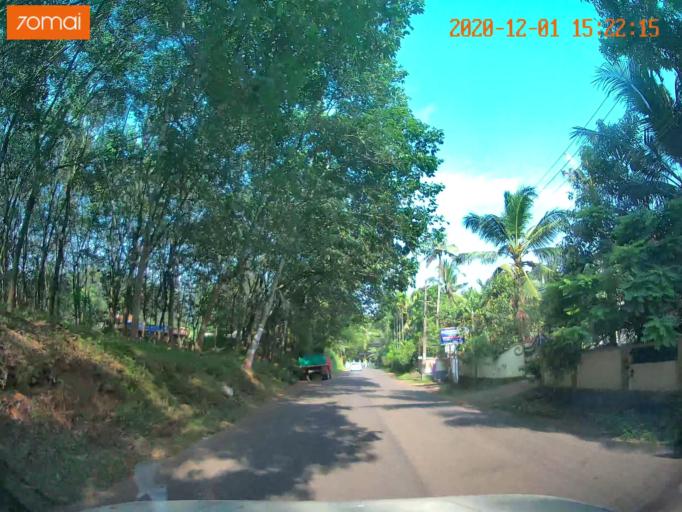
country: IN
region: Kerala
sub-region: Ernakulam
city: Muvattupuzha
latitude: 9.9458
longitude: 76.5473
